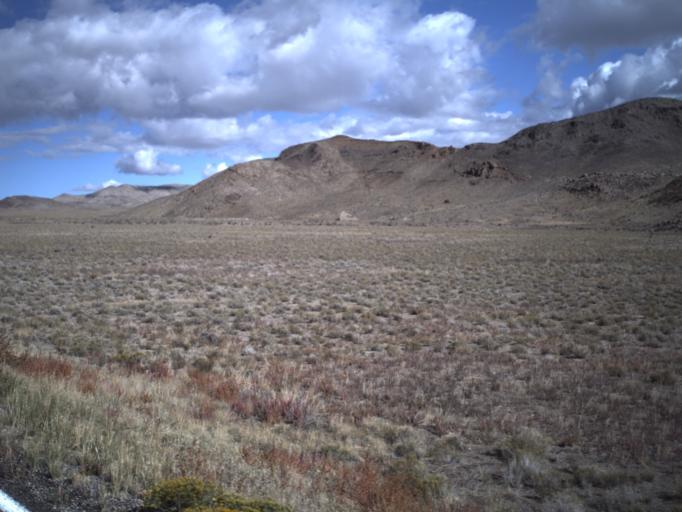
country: US
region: Utah
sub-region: Beaver County
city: Milford
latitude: 38.5800
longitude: -113.8071
